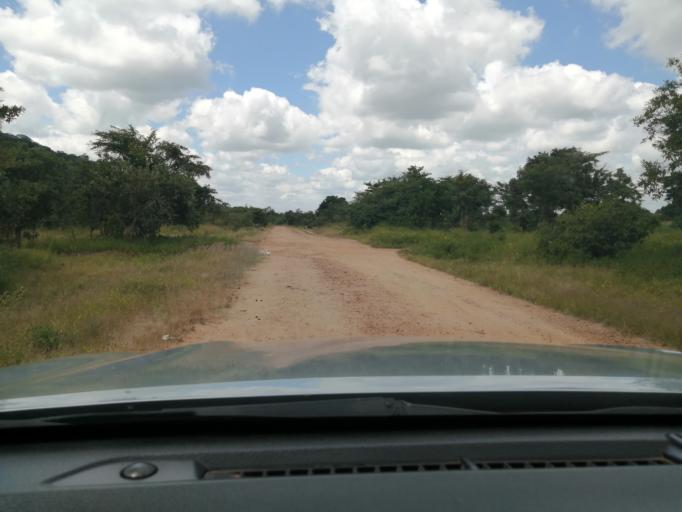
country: ZM
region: Lusaka
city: Lusaka
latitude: -15.1386
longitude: 27.9225
